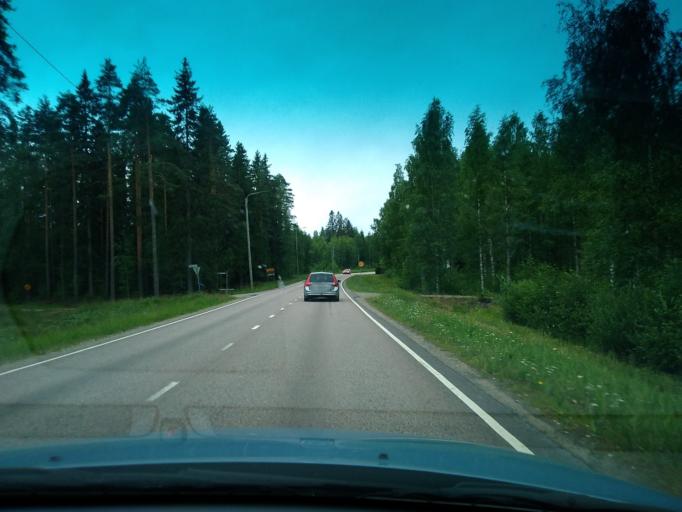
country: FI
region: Central Finland
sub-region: Keuruu
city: Multia
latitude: 62.3992
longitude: 24.7902
